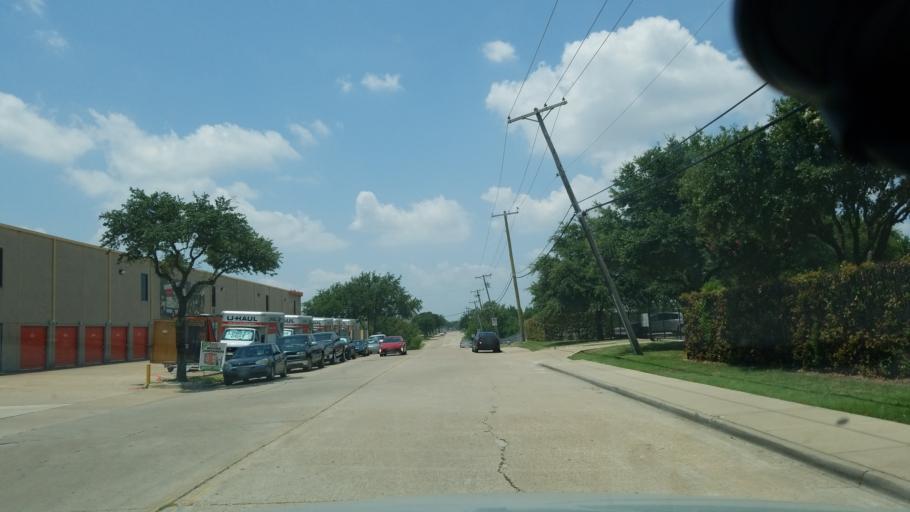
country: US
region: Texas
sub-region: Dallas County
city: Carrollton
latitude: 32.9609
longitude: -96.8782
